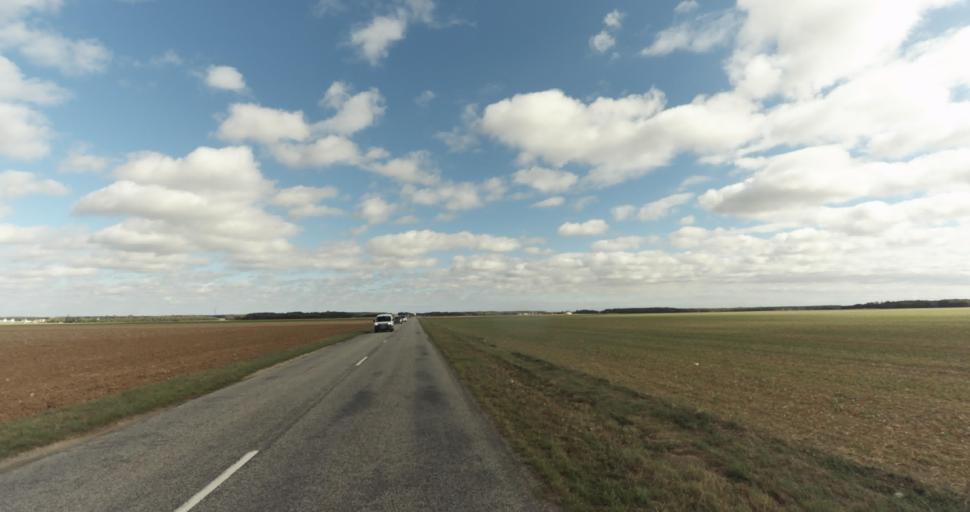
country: FR
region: Centre
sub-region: Departement d'Eure-et-Loir
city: Garnay
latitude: 48.7071
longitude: 1.3021
